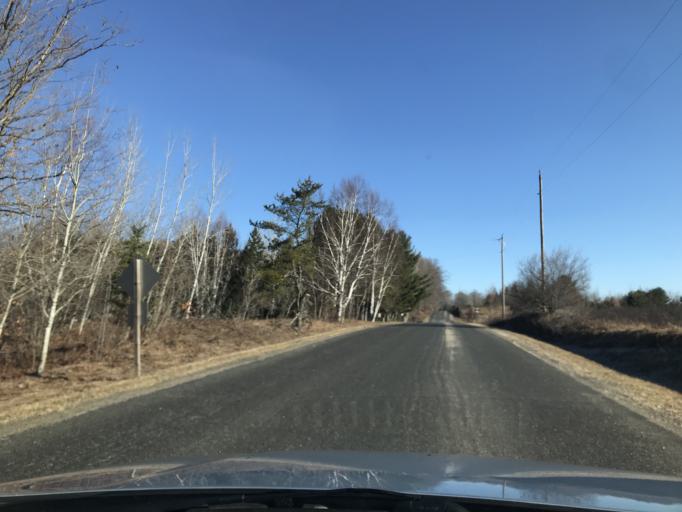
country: US
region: Wisconsin
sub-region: Marinette County
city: Niagara
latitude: 45.3704
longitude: -88.0193
